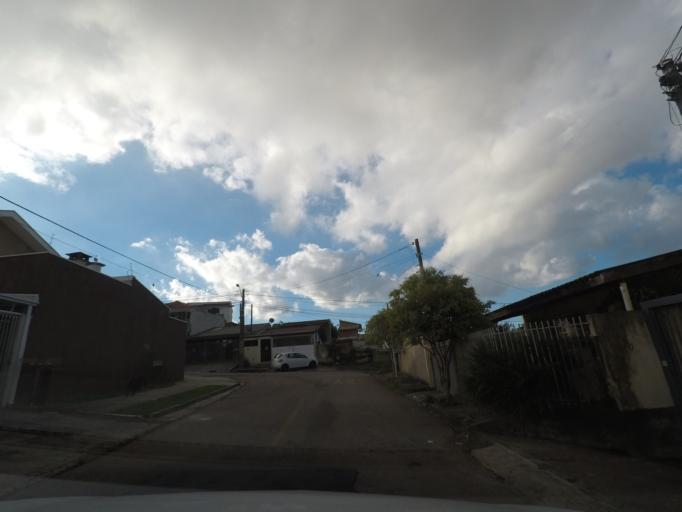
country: BR
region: Parana
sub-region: Sao Jose Dos Pinhais
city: Sao Jose dos Pinhais
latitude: -25.5024
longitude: -49.2596
